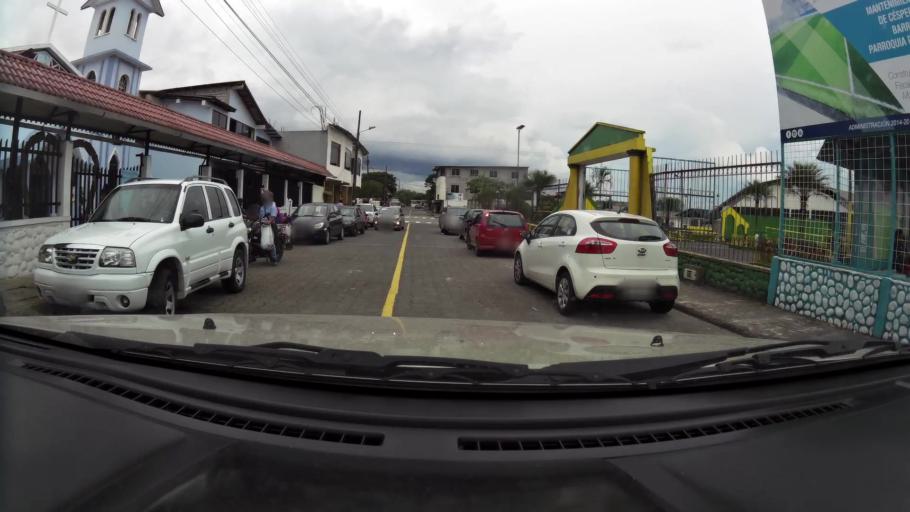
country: EC
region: Pastaza
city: Puyo
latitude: -1.4919
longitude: -78.0121
